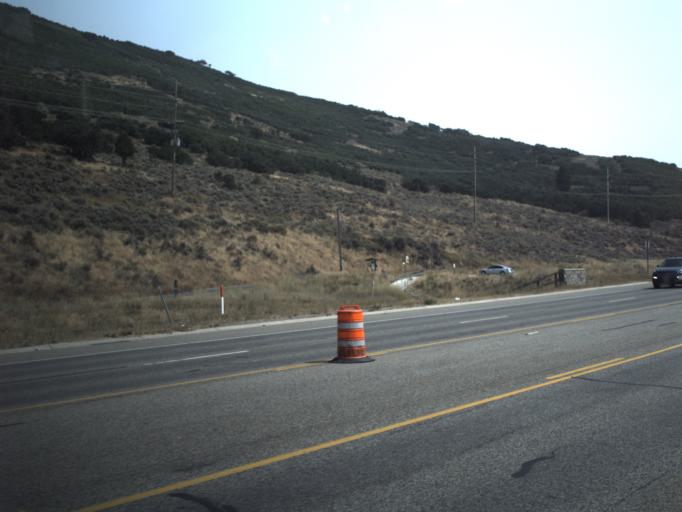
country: US
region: Utah
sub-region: Summit County
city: Snyderville
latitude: 40.6785
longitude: -111.5268
